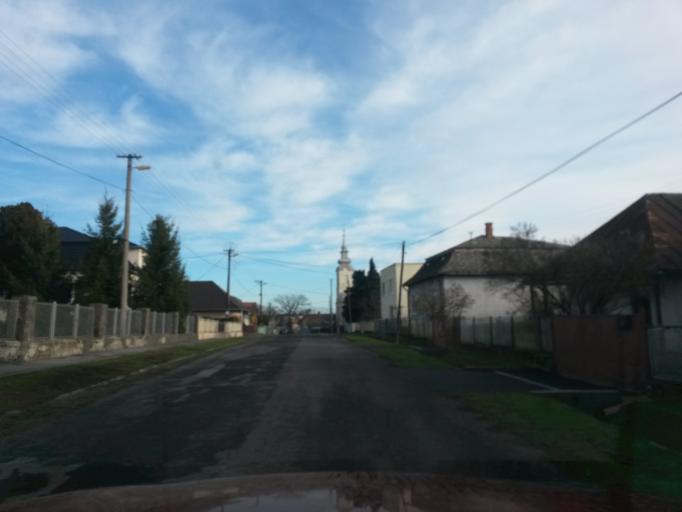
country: SK
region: Kosicky
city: Cierna nad Tisou
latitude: 48.5396
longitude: 22.0229
